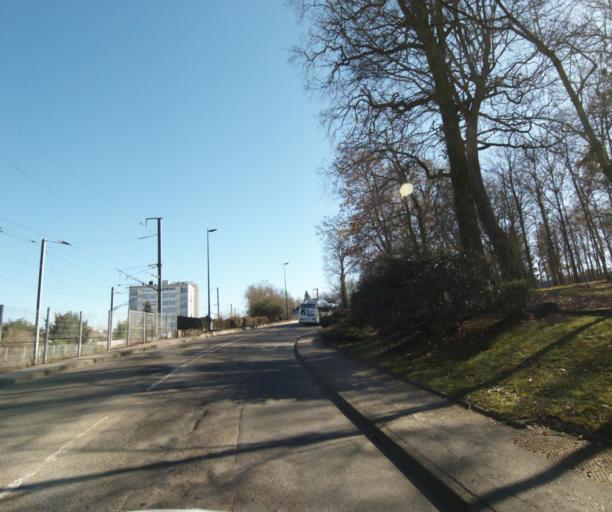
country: FR
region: Lorraine
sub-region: Departement de Meurthe-et-Moselle
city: Jarville-la-Malgrange
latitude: 48.6676
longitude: 6.2076
